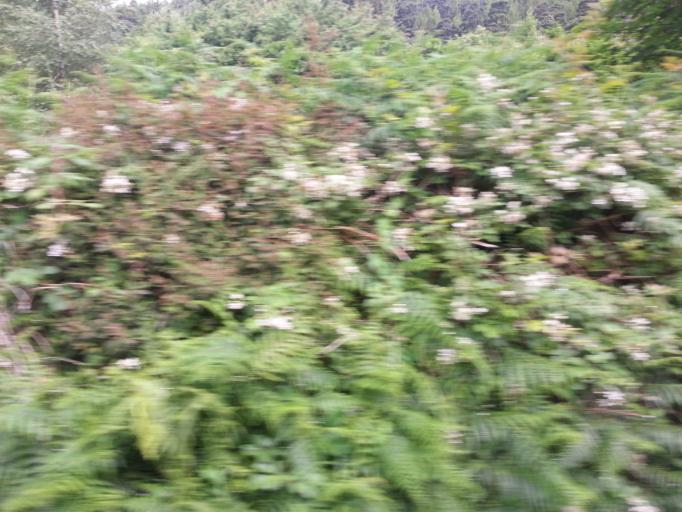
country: IE
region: Leinster
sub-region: Wicklow
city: Rathdrum
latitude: 53.0090
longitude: -6.3393
